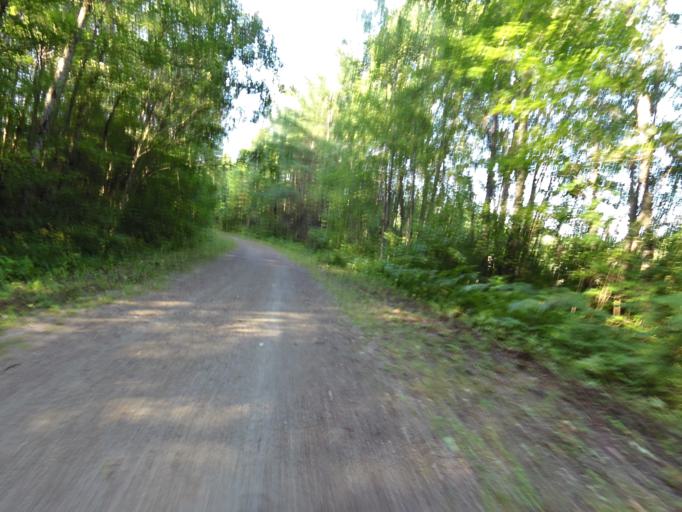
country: CA
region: Quebec
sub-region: Outaouais
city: Maniwaki
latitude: 46.2630
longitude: -76.0236
